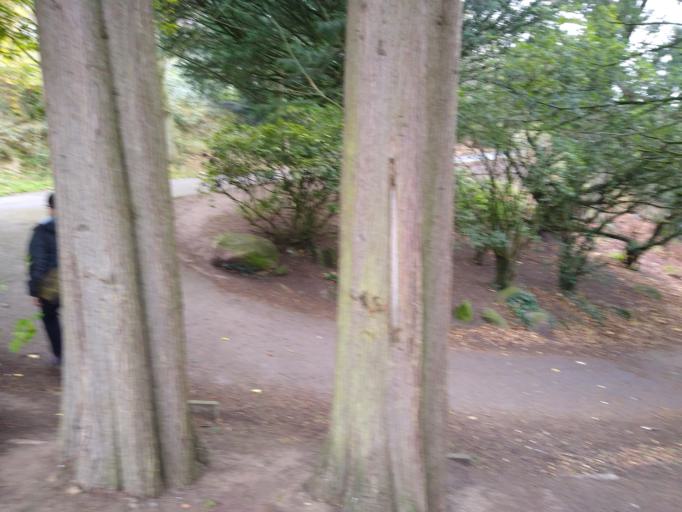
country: GB
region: England
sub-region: Redcar and Cleveland
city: Saltburn-by-the-Sea
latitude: 54.5787
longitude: -0.9721
